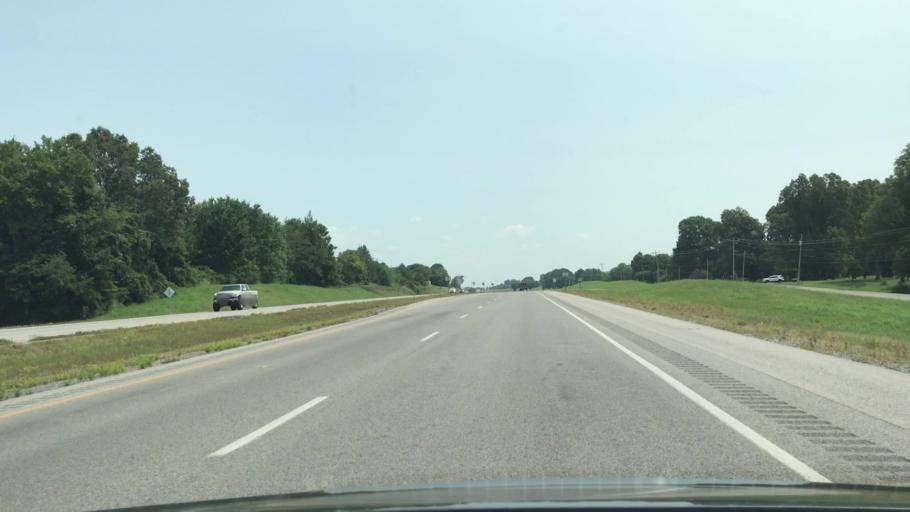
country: US
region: Kentucky
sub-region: Trigg County
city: Cadiz
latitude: 36.8694
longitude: -87.7720
